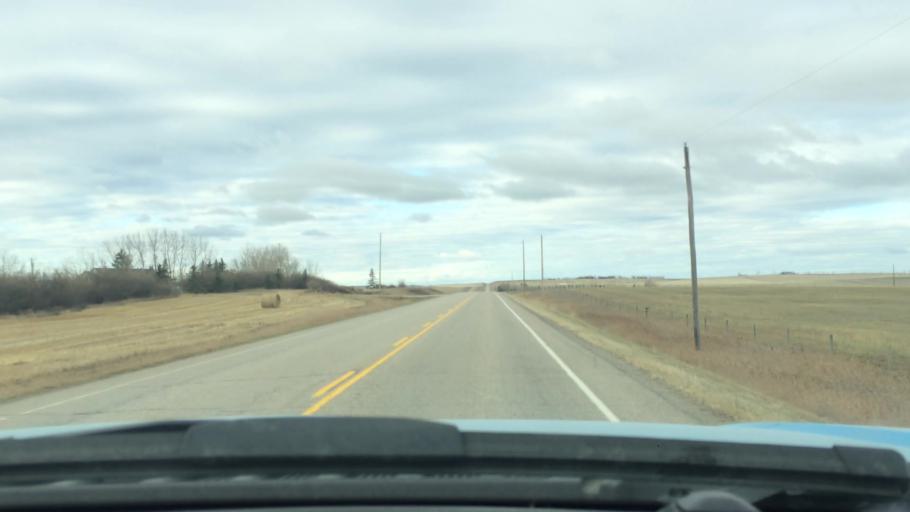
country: CA
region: Alberta
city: Airdrie
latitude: 51.2125
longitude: -114.0754
